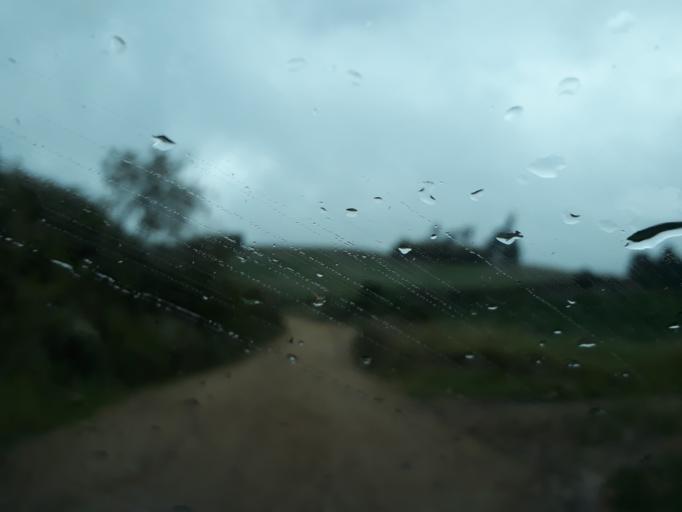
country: CO
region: Cundinamarca
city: Villapinzon
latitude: 5.2933
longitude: -73.6213
